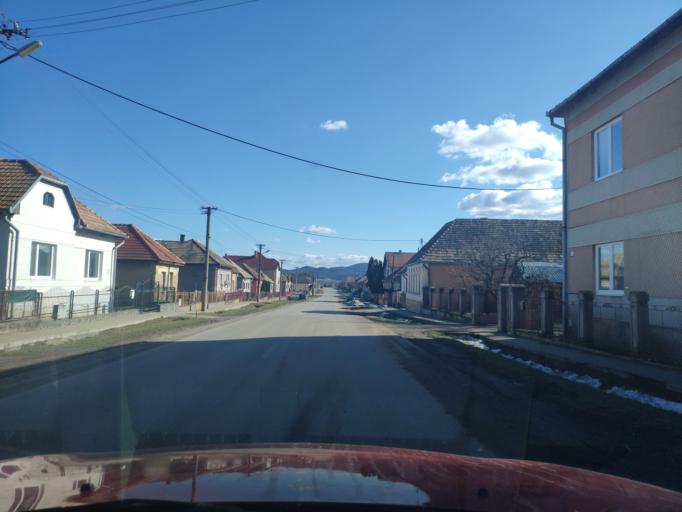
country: SK
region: Banskobystricky
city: Rimavska Sobota
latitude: 48.2895
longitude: 20.0878
